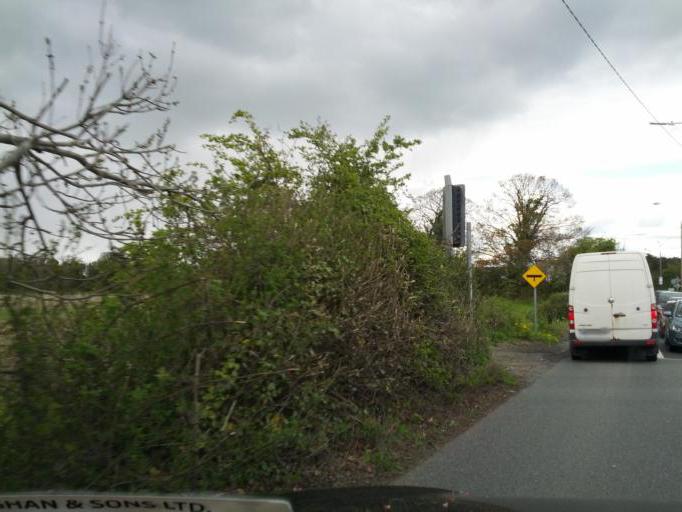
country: IE
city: Confey
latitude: 53.3746
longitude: -6.4848
